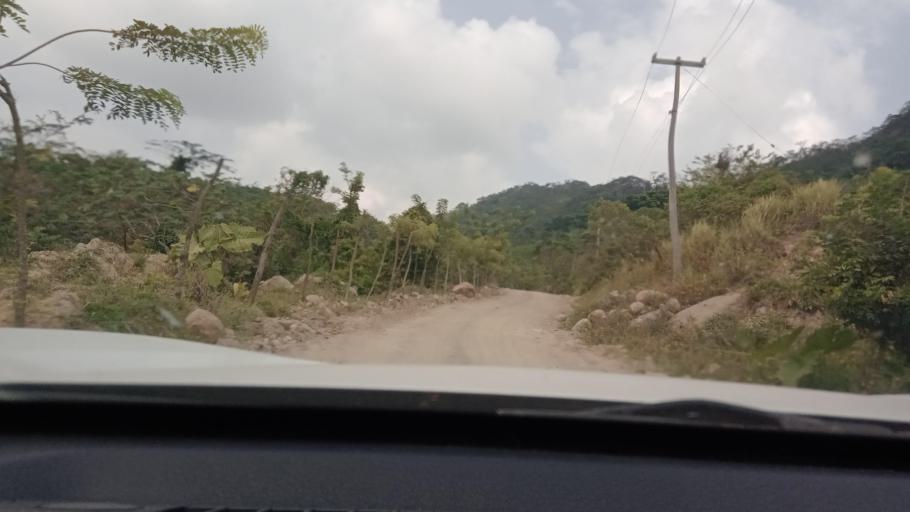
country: MX
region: Tabasco
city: Chontalpa
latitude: 17.4943
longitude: -93.6577
